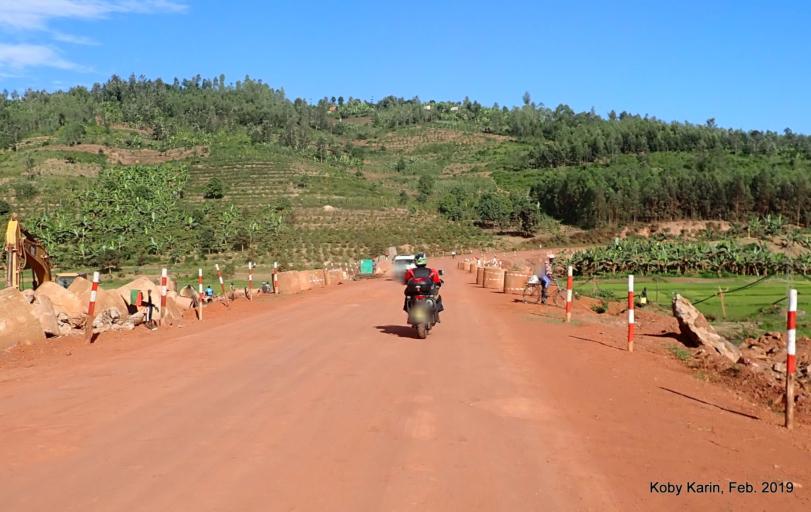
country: RW
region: Eastern Province
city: Kibungo
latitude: -2.2747
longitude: 30.5551
